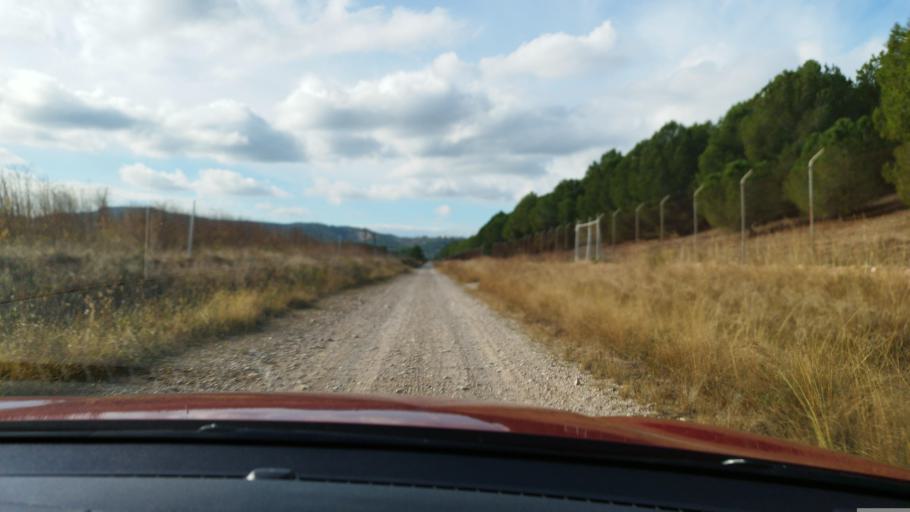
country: ES
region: Catalonia
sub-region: Provincia de Tarragona
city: Santa Oliva
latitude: 41.2592
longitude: 1.5223
